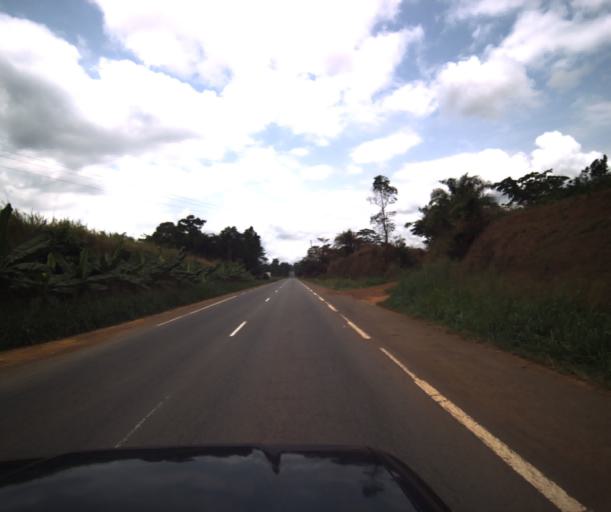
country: CM
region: Centre
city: Eseka
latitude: 3.8712
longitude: 10.9070
